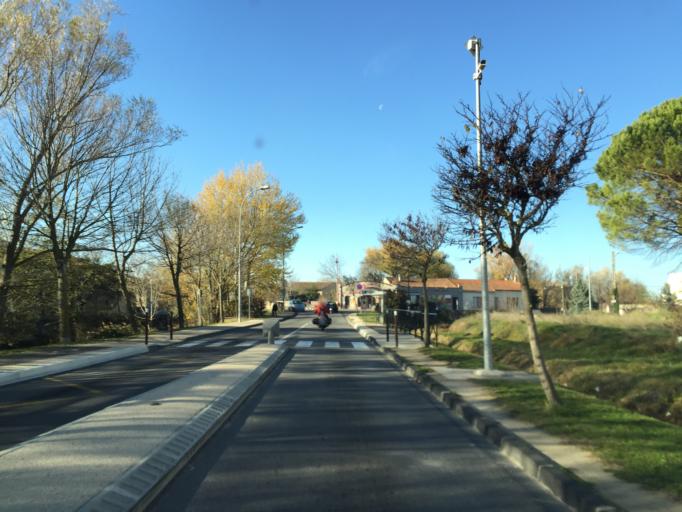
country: FR
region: Provence-Alpes-Cote d'Azur
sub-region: Departement du Vaucluse
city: Entraigues-sur-la-Sorgue
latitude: 44.0050
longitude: 4.9323
